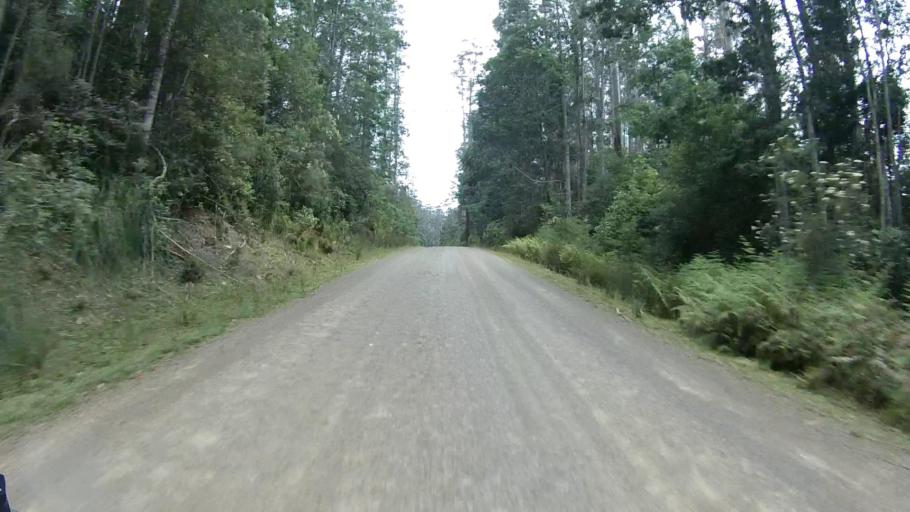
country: AU
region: Tasmania
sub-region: Sorell
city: Sorell
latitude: -42.7153
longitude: 147.8417
